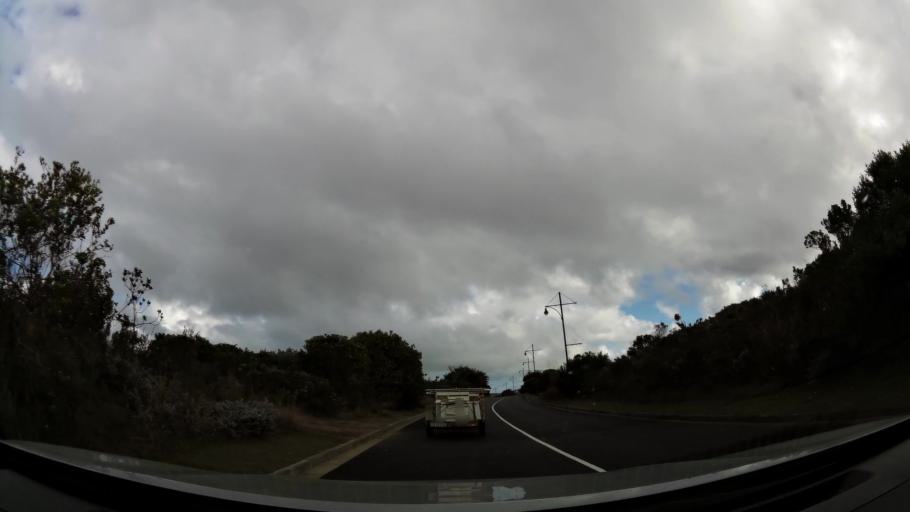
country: ZA
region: Western Cape
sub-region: Eden District Municipality
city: Knysna
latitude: -34.0690
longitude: 23.0913
